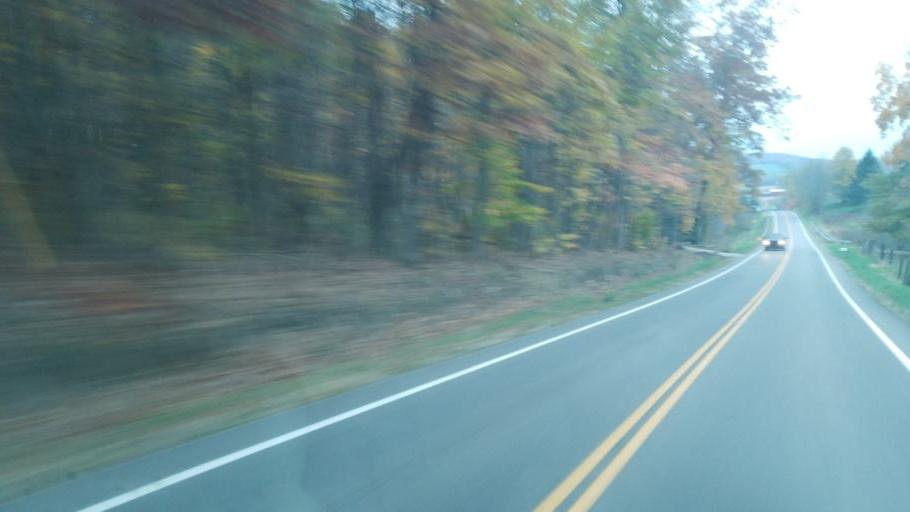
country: US
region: Ohio
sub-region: Sandusky County
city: Bellville
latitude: 40.6151
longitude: -82.4062
